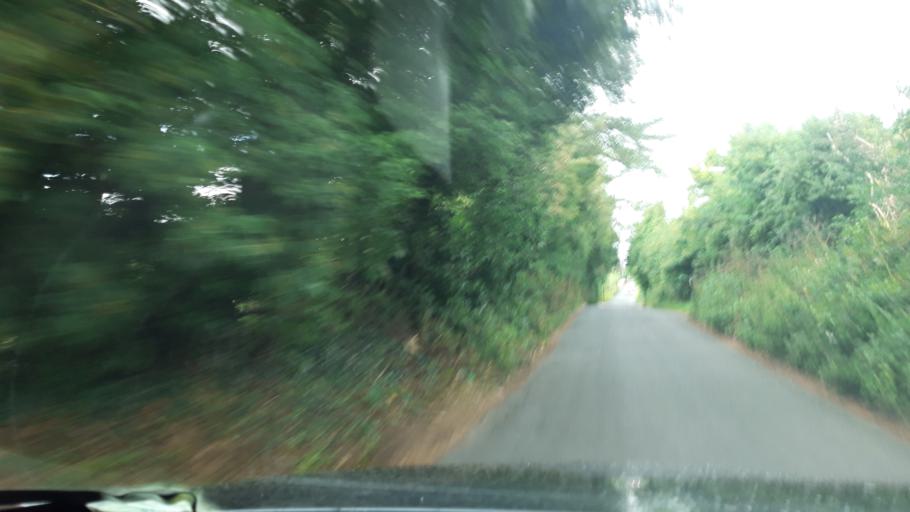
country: IE
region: Leinster
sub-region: Wicklow
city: Baltinglass
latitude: 52.9465
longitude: -6.7068
